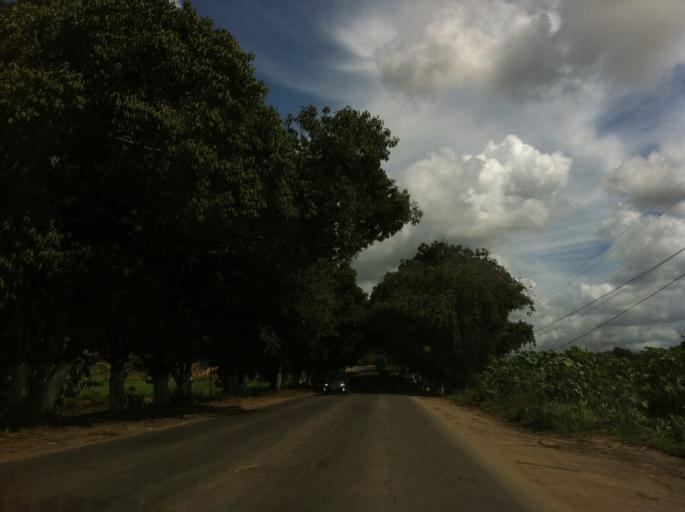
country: BR
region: Alagoas
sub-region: Sao Luis Do Quitunde
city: Sao Luis do Quitunde
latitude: -9.2944
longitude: -35.5656
